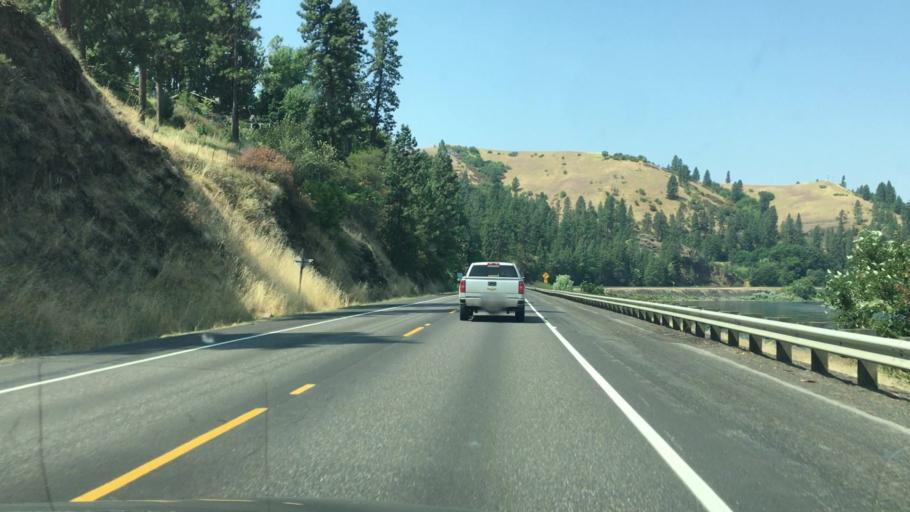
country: US
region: Idaho
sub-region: Nez Perce County
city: Lapwai
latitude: 46.5058
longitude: -116.5425
